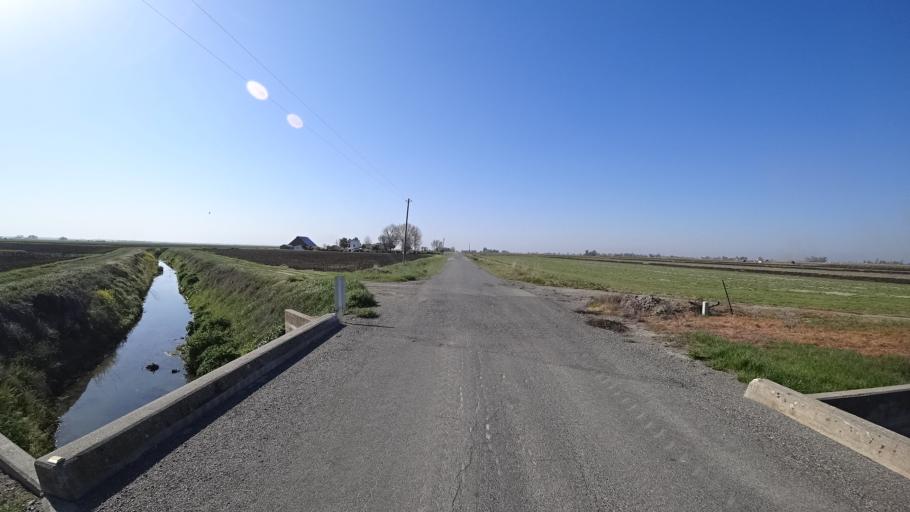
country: US
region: California
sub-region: Glenn County
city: Willows
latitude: 39.5717
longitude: -122.0839
